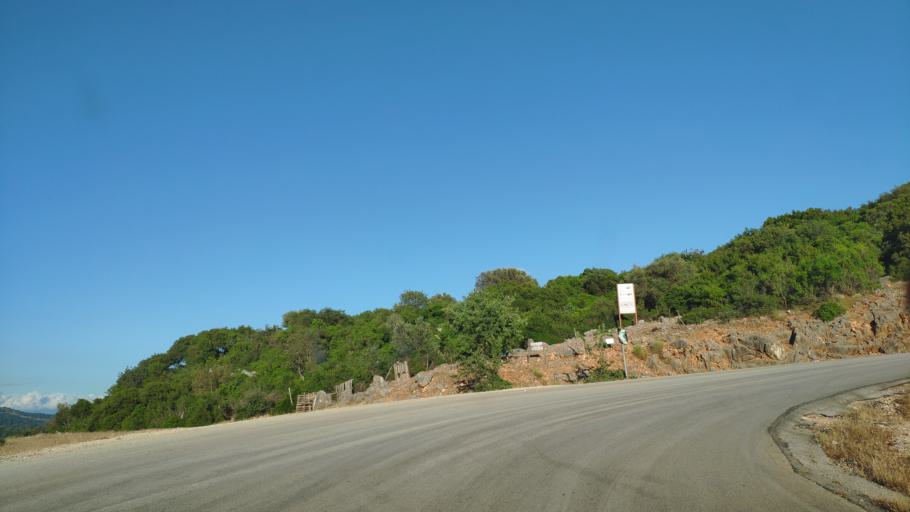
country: GR
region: West Greece
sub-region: Nomos Aitolias kai Akarnanias
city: Astakos
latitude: 38.6091
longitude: 21.1354
